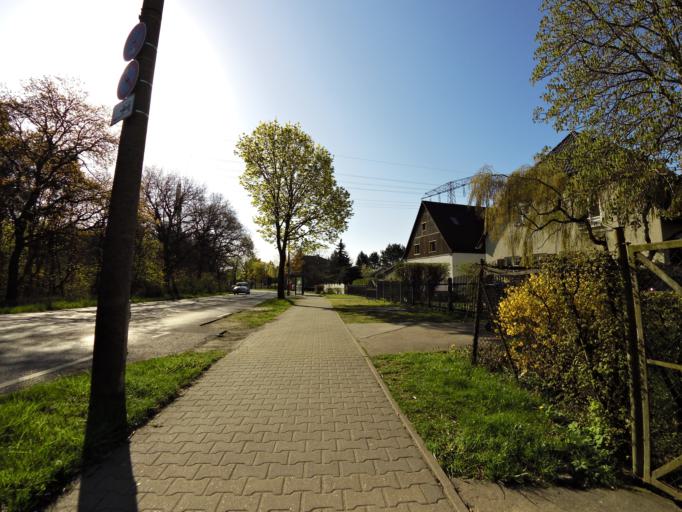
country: DE
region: Berlin
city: Baumschulenweg
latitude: 52.4529
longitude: 13.4807
